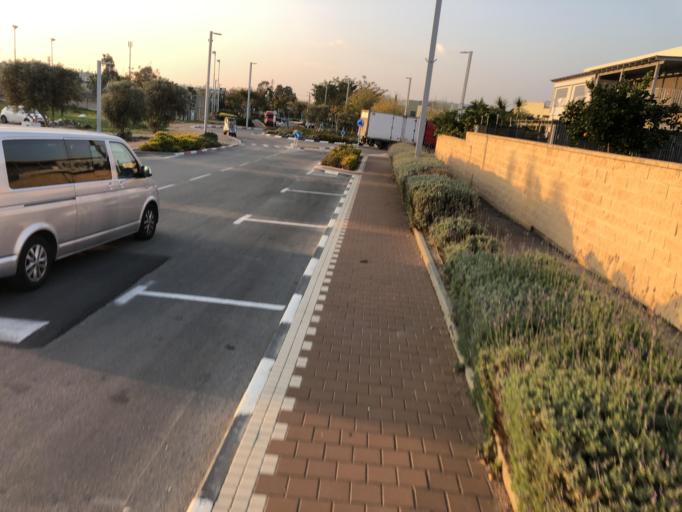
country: IL
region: Northern District
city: `Akko
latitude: 32.9285
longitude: 35.0857
